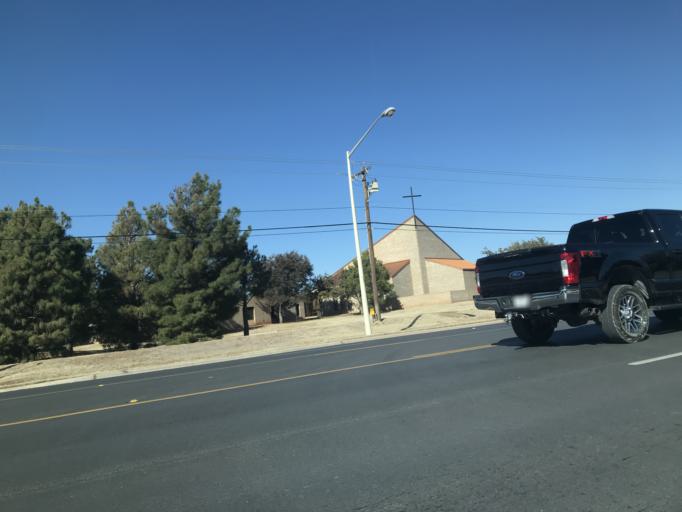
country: US
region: Texas
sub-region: Taylor County
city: Abilene
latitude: 32.3829
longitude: -99.7692
